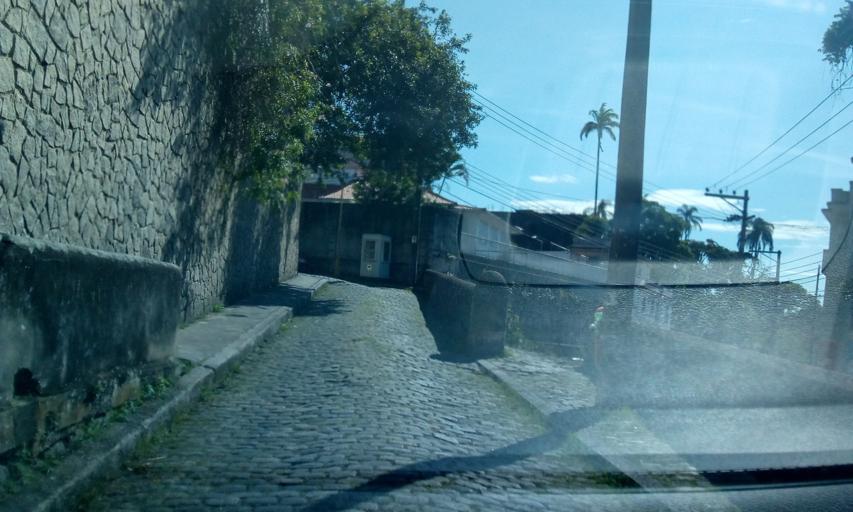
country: BR
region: Rio de Janeiro
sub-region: Rio De Janeiro
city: Rio de Janeiro
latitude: -22.9180
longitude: -43.1816
